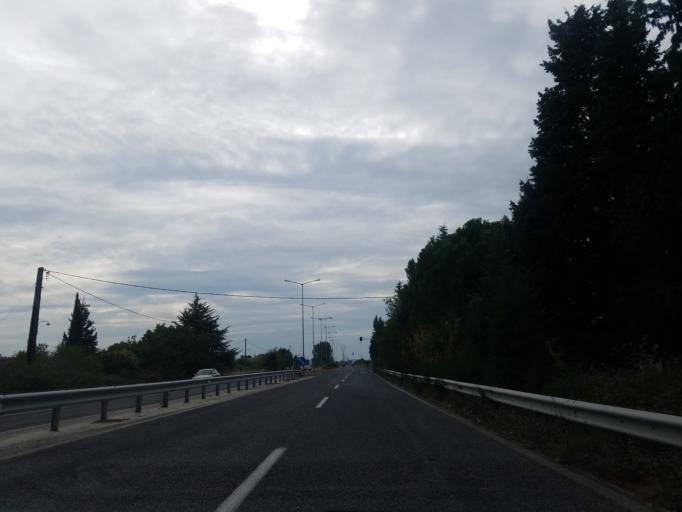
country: GR
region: Thessaly
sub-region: Trikala
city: Vasiliki
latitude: 39.6367
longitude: 21.6974
